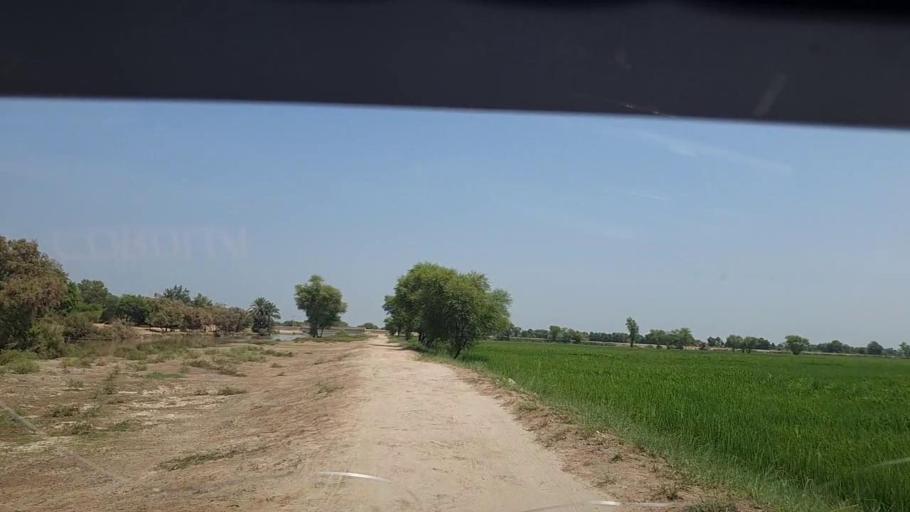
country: PK
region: Sindh
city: Tangwani
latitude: 28.2296
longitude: 68.9276
